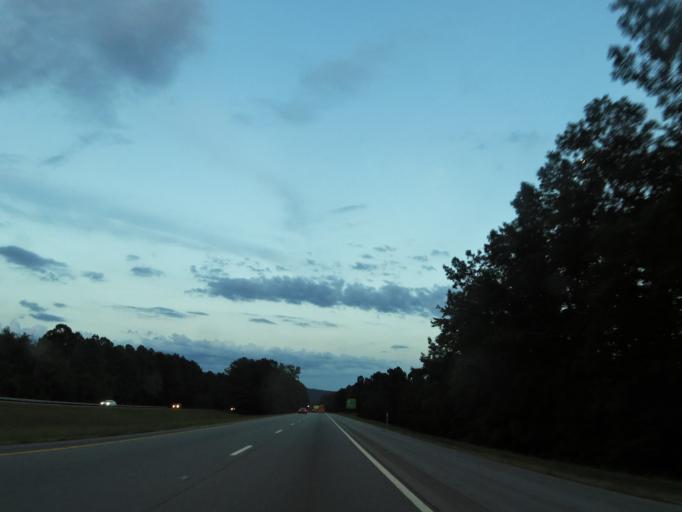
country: US
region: Tennessee
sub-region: Roane County
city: Rockwood
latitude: 35.8946
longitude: -84.7557
